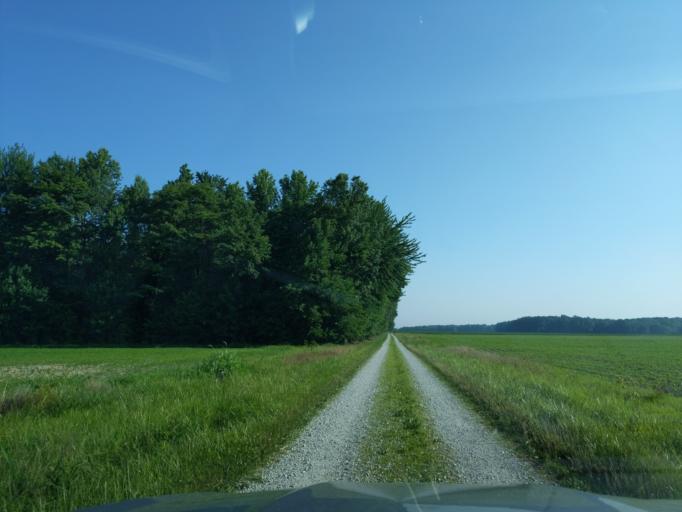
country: US
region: Indiana
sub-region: Decatur County
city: Greensburg
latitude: 39.2136
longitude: -85.4208
